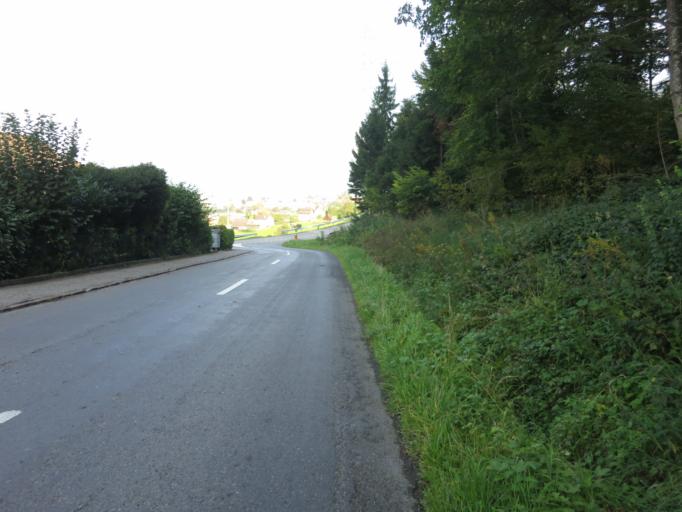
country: CH
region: Schwyz
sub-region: Bezirk March
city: Lachen
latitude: 47.1717
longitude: 8.8794
